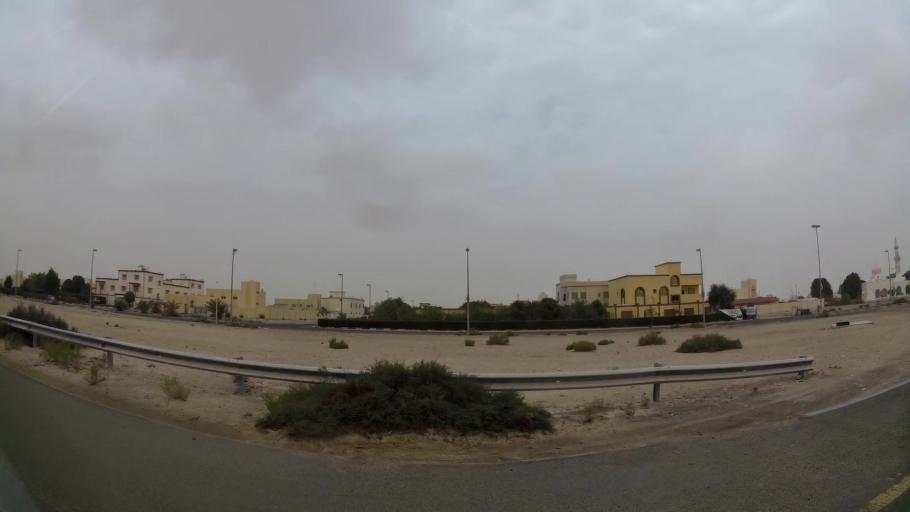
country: AE
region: Abu Dhabi
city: Abu Dhabi
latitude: 24.3955
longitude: 54.7457
